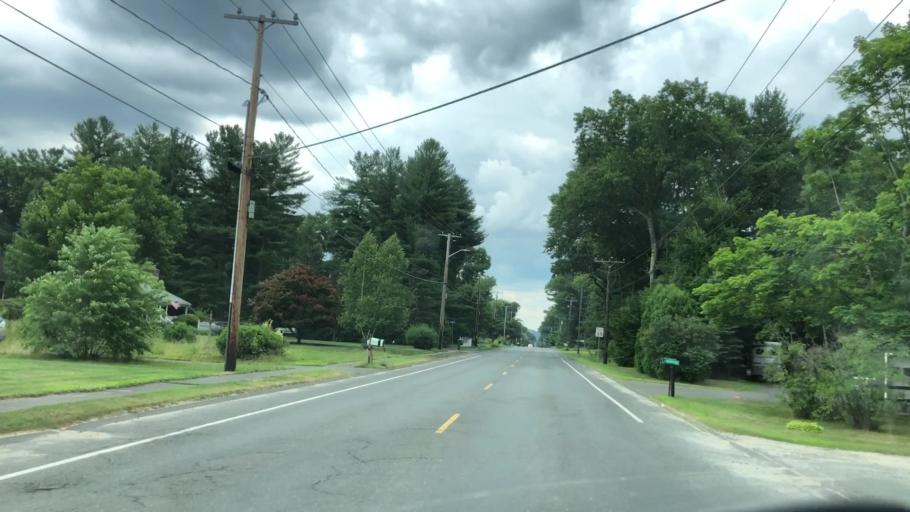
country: US
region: Massachusetts
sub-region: Hampshire County
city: Southampton
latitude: 42.2091
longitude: -72.6899
